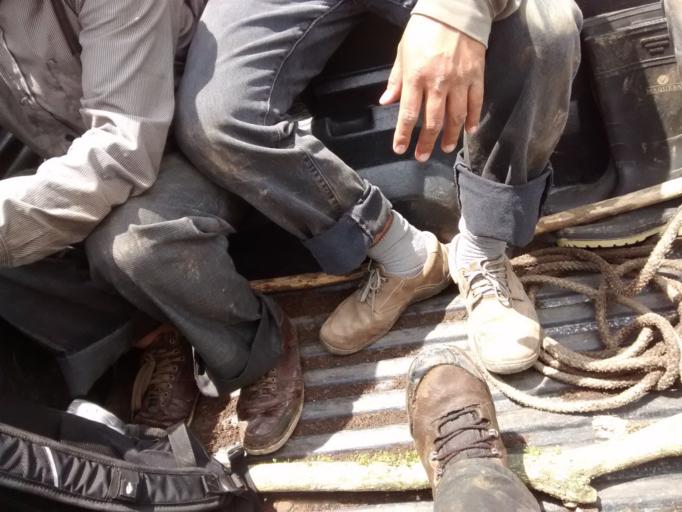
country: GT
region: Sacatepequez
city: Santo Domingo Xenacoj
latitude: 14.6903
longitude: -90.7090
